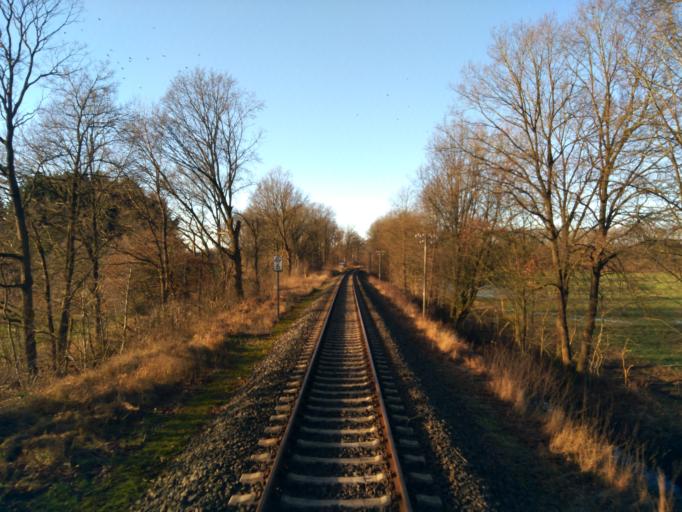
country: DE
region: Lower Saxony
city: Soltau
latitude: 52.9780
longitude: 9.8679
